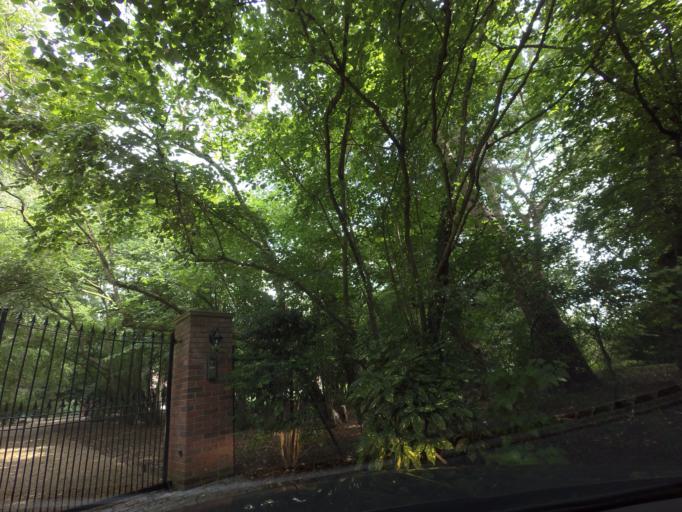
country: GB
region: England
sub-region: Kent
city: Boxley
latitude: 51.2800
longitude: 0.5819
